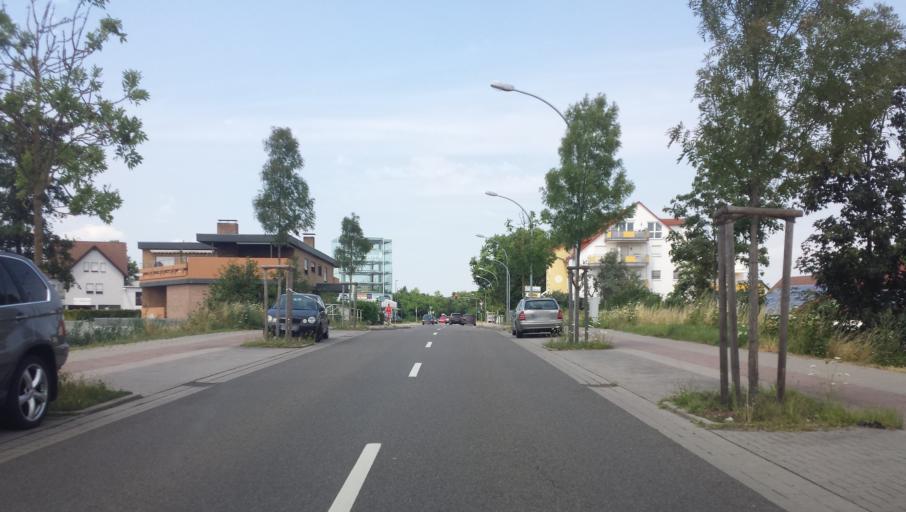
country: DE
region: Rheinland-Pfalz
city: Speyer
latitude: 49.3400
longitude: 8.4323
